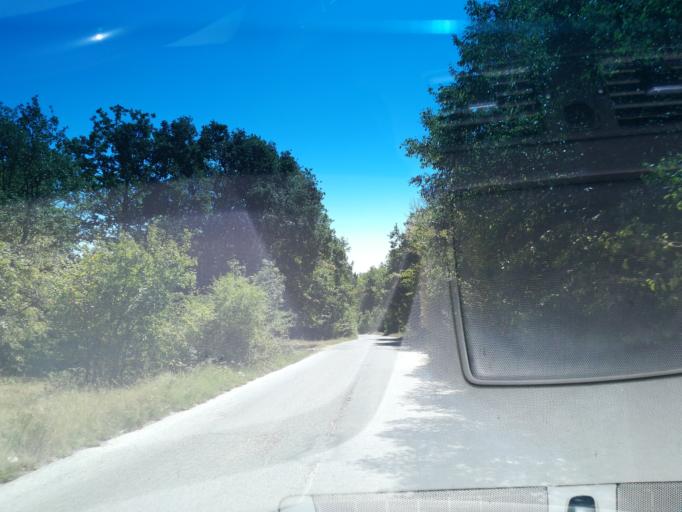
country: BG
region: Pazardzhik
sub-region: Obshtina Strelcha
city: Strelcha
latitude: 42.5463
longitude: 24.3287
